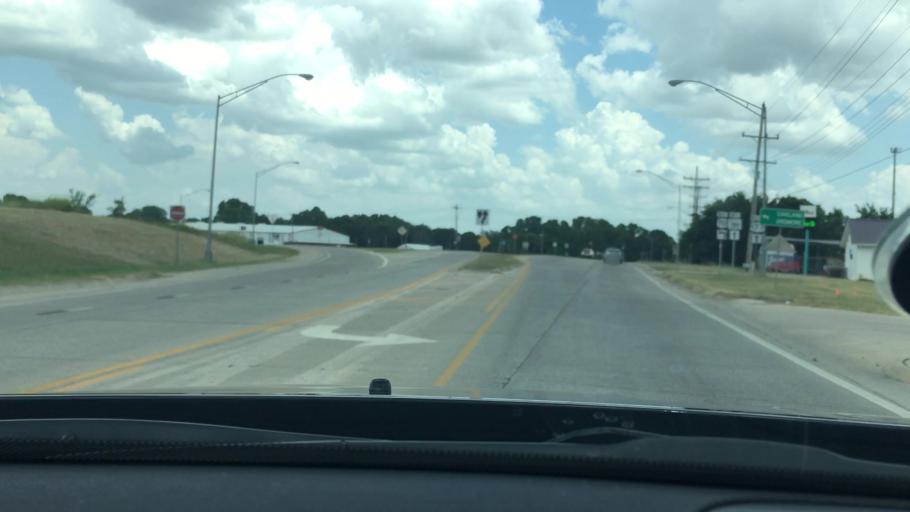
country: US
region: Oklahoma
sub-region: Marshall County
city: Madill
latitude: 34.0982
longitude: -96.7752
